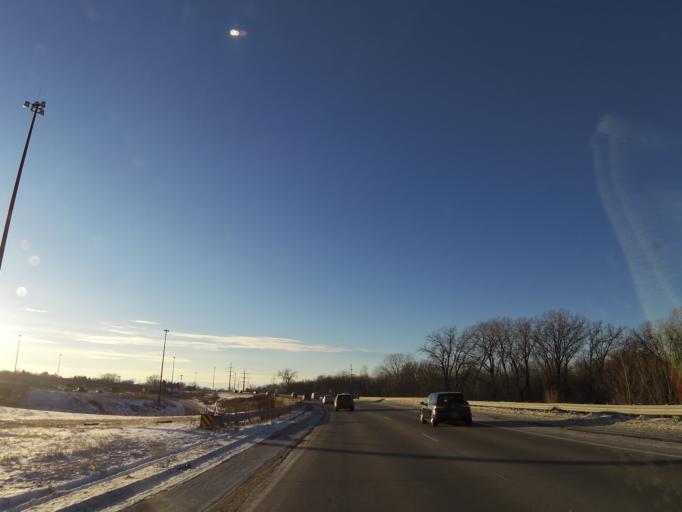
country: US
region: Minnesota
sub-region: Hennepin County
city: Eden Prairie
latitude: 44.8622
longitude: -93.4689
